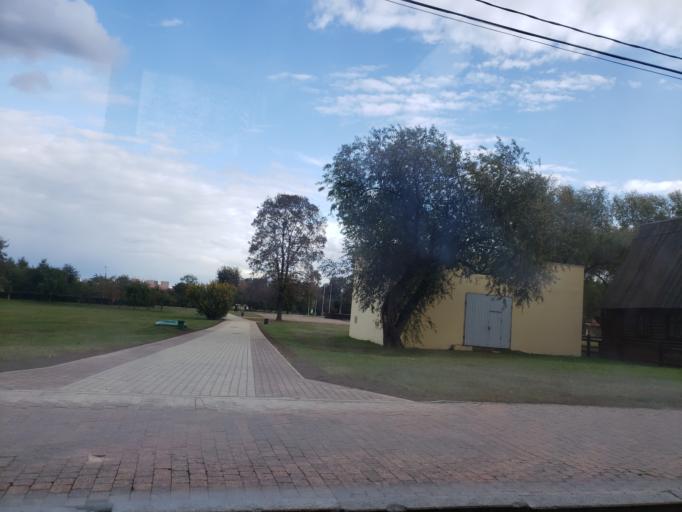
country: RU
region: Moscow
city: Kolomenskoye
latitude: 55.6721
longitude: 37.6690
